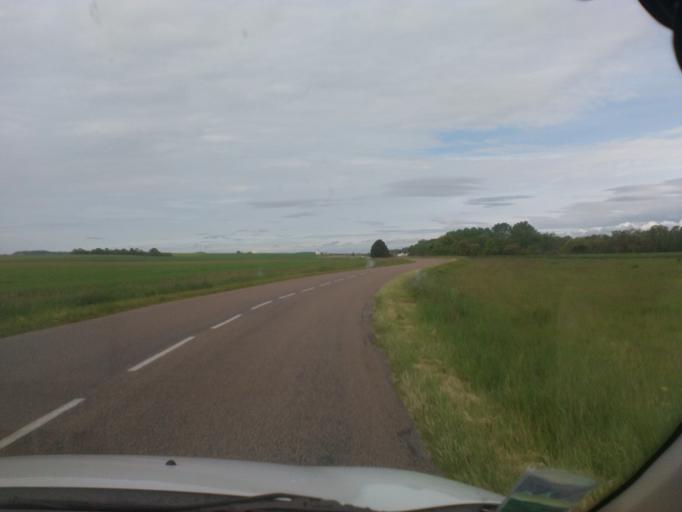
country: FR
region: Champagne-Ardenne
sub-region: Departement de l'Aube
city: Marigny-le-Chatel
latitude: 48.3559
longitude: 3.6792
